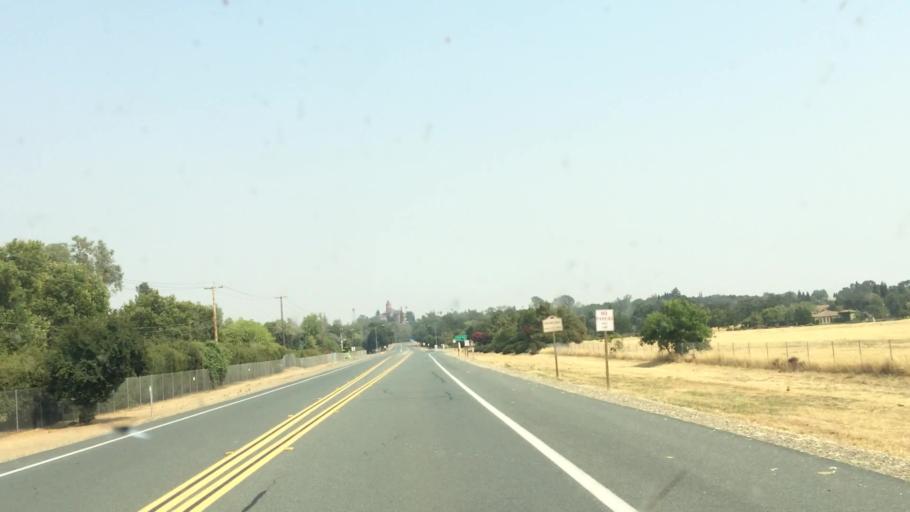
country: US
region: California
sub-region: Amador County
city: Ione
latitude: 38.3661
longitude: -120.9523
